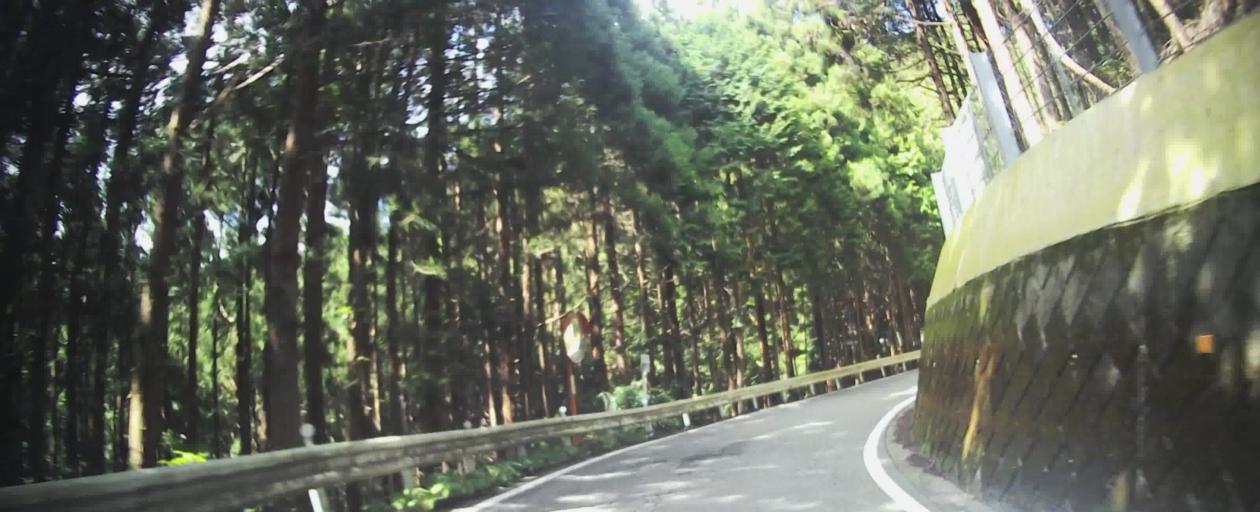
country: JP
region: Gunma
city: Shibukawa
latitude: 36.4533
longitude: 138.8994
